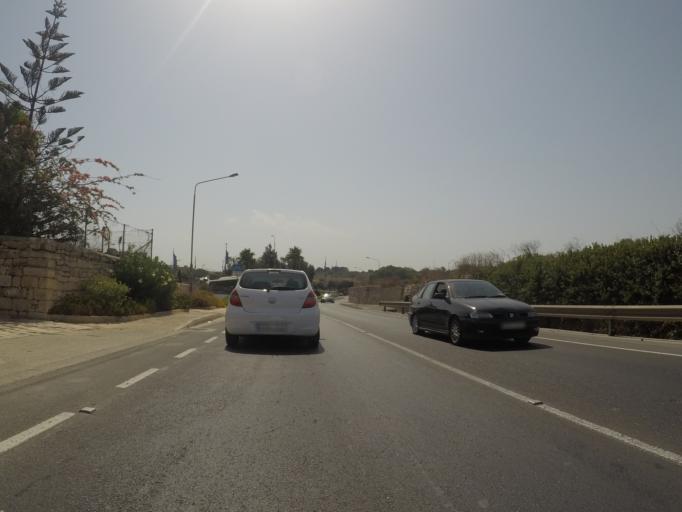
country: MT
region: L-Imtarfa
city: Imtarfa
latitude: 35.9048
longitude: 14.4079
